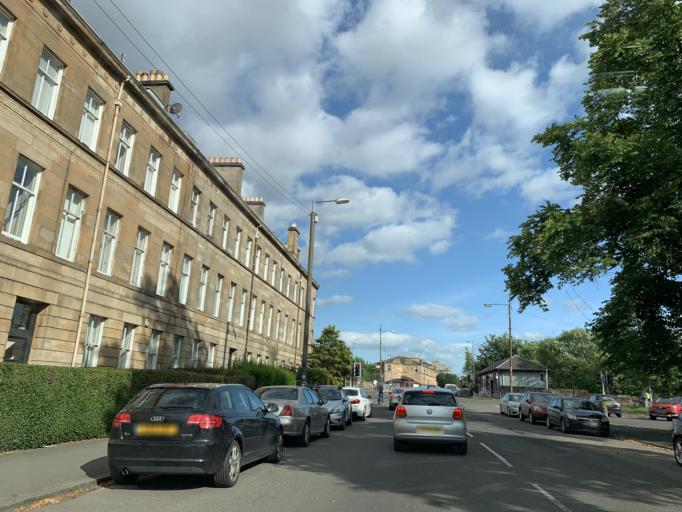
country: GB
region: Scotland
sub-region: Glasgow City
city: Glasgow
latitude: 55.8384
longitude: -4.2741
